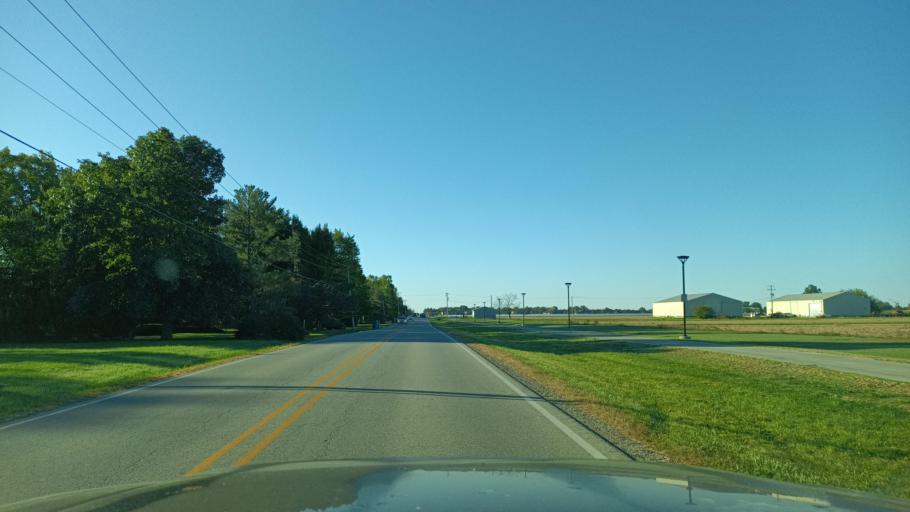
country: US
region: Illinois
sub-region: Champaign County
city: Savoy
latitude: 40.0787
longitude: -88.2385
